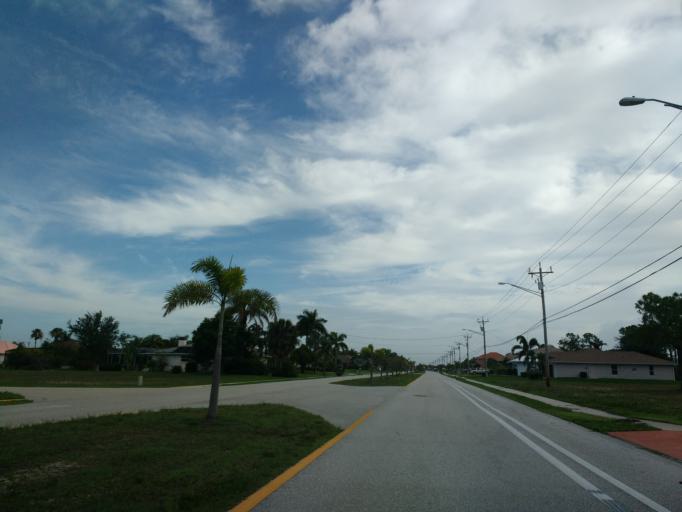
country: US
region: Florida
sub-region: Lee County
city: Cape Coral
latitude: 26.5817
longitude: -82.0240
